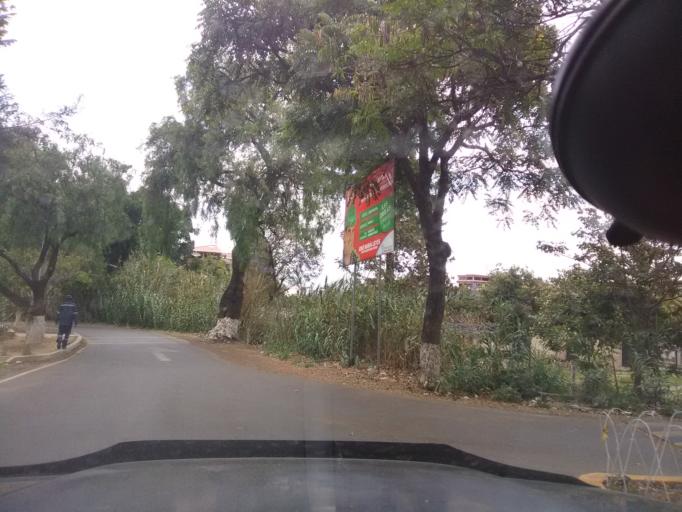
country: BO
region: Cochabamba
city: Cochabamba
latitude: -17.3643
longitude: -66.1689
